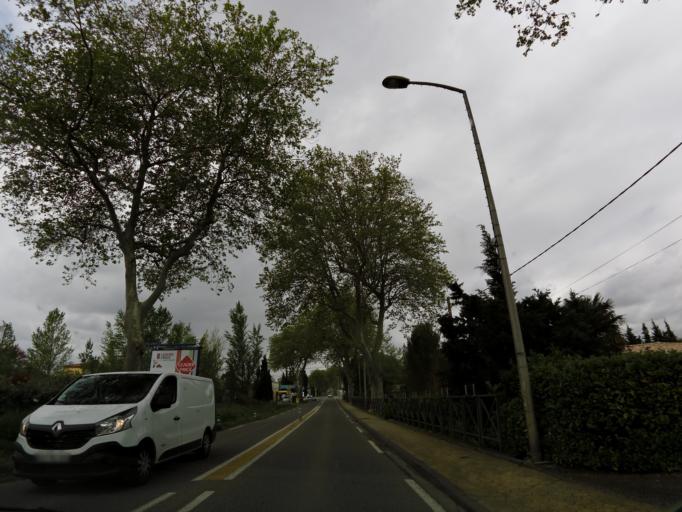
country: FR
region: Languedoc-Roussillon
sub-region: Departement de l'Aude
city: Castelnaudary
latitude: 43.3126
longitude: 1.9670
